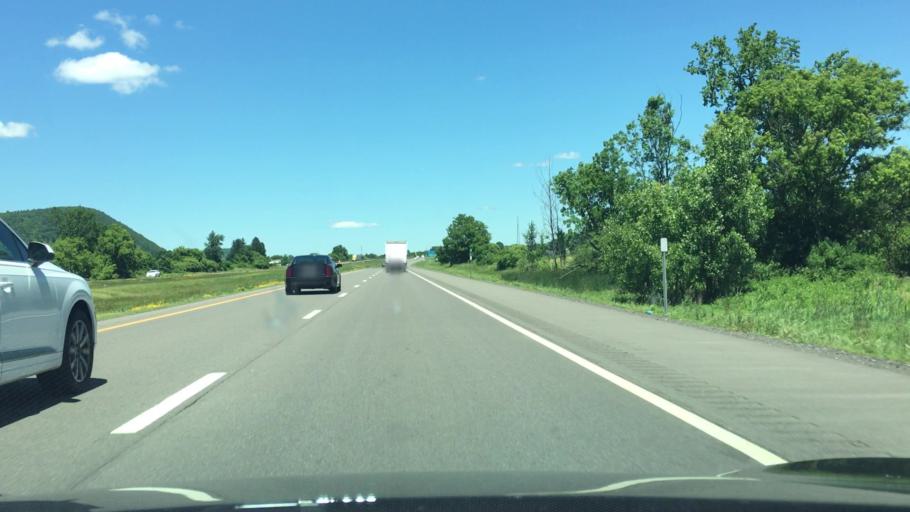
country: US
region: New York
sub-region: Cortland County
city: Homer
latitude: 42.6887
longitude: -76.1603
